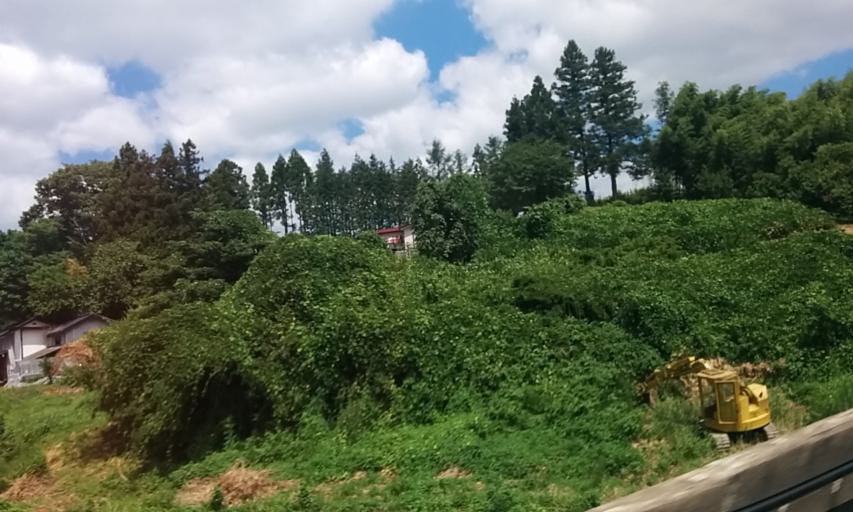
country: JP
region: Fukushima
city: Motomiya
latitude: 37.5142
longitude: 140.4311
